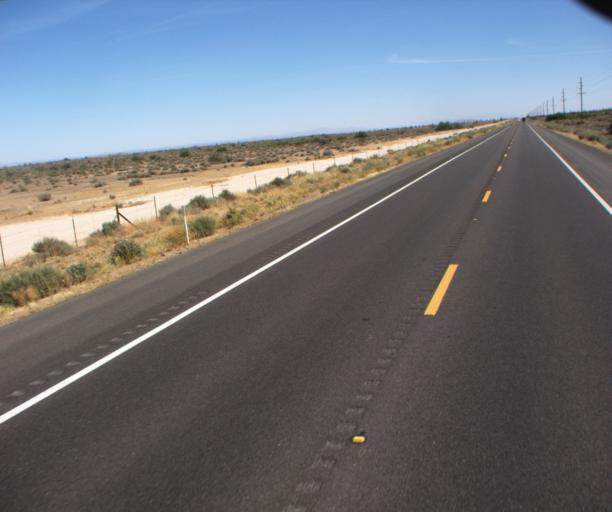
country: US
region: Arizona
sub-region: Pinal County
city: Blackwater
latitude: 33.0391
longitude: -111.6594
